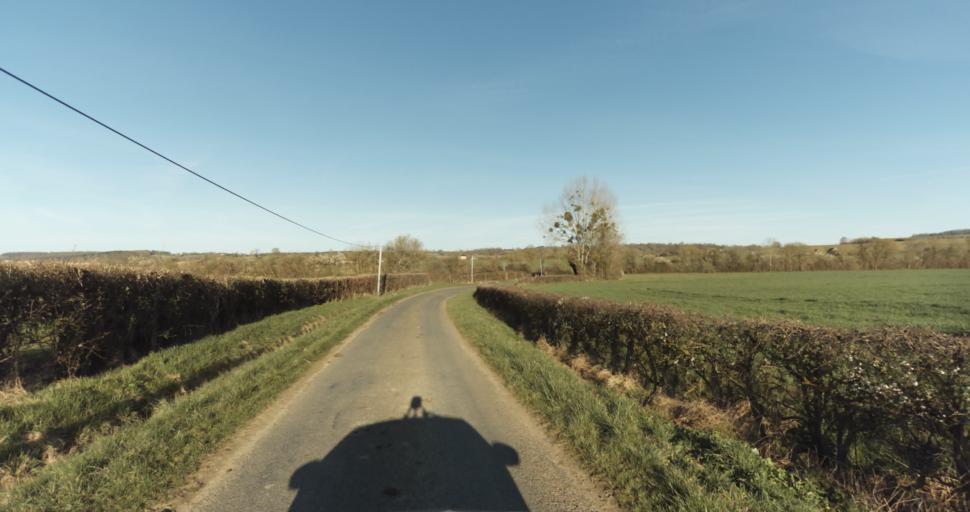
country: FR
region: Lower Normandy
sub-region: Departement de l'Orne
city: Trun
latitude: 48.9154
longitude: 0.0235
